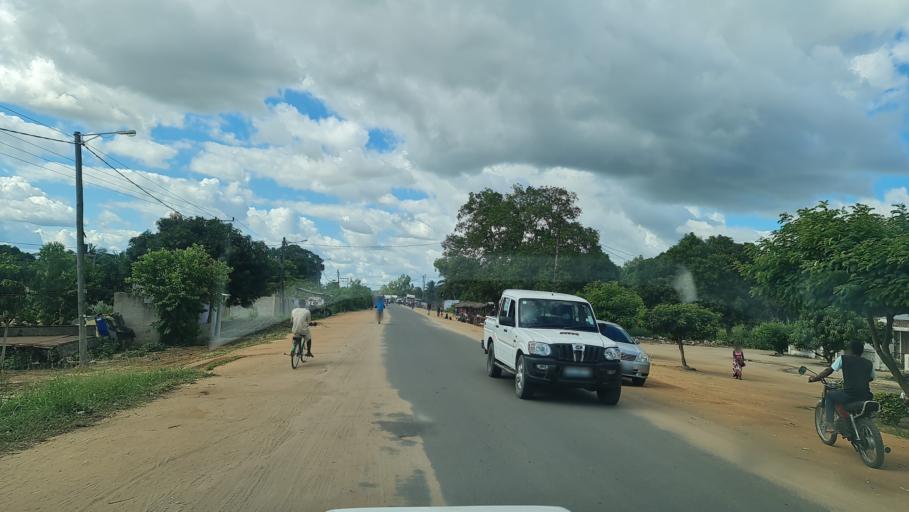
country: MZ
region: Zambezia
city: Quelimane
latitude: -17.5974
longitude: 36.8104
